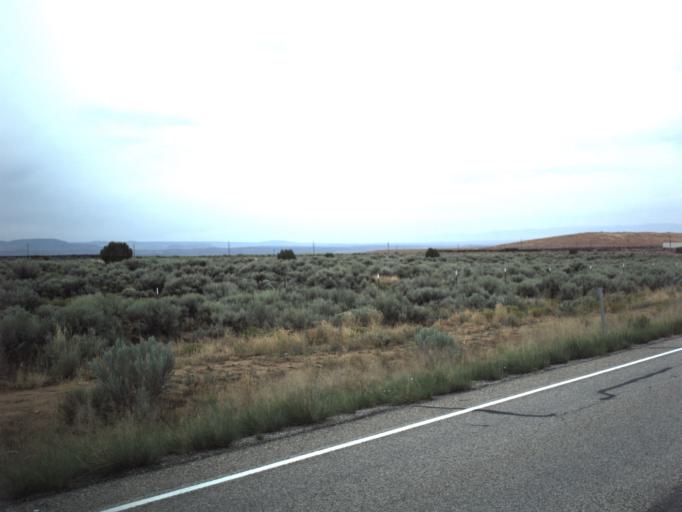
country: US
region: Utah
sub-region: Carbon County
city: East Carbon City
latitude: 39.5371
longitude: -110.4546
